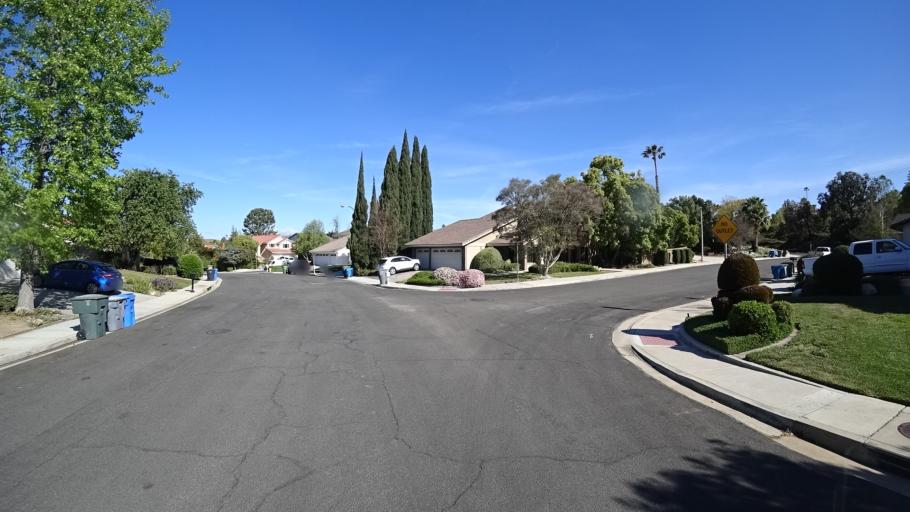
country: US
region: California
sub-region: Ventura County
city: Thousand Oaks
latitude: 34.2268
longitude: -118.8560
